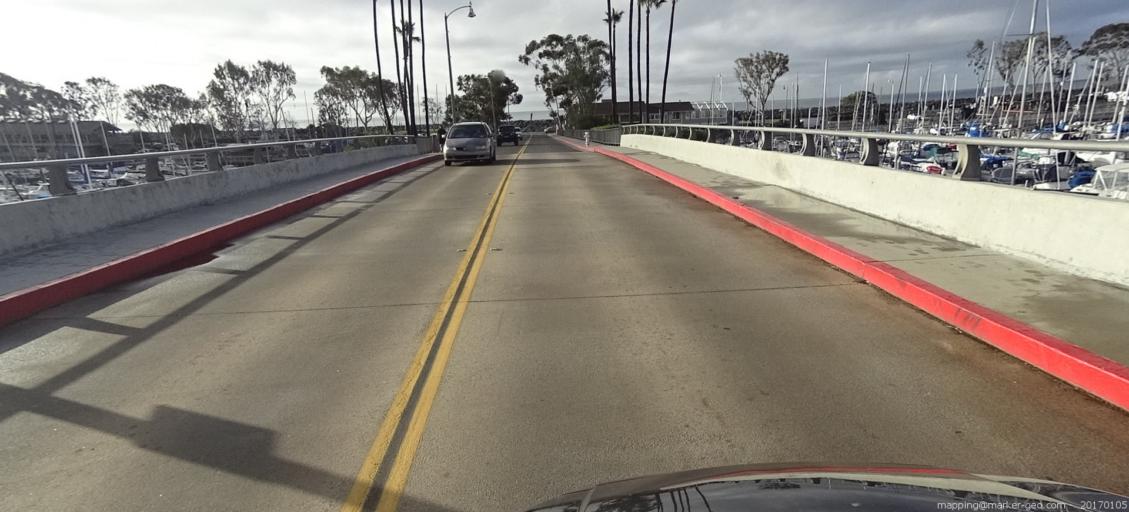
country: US
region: California
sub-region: Orange County
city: Dana Point
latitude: 33.4603
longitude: -117.6993
